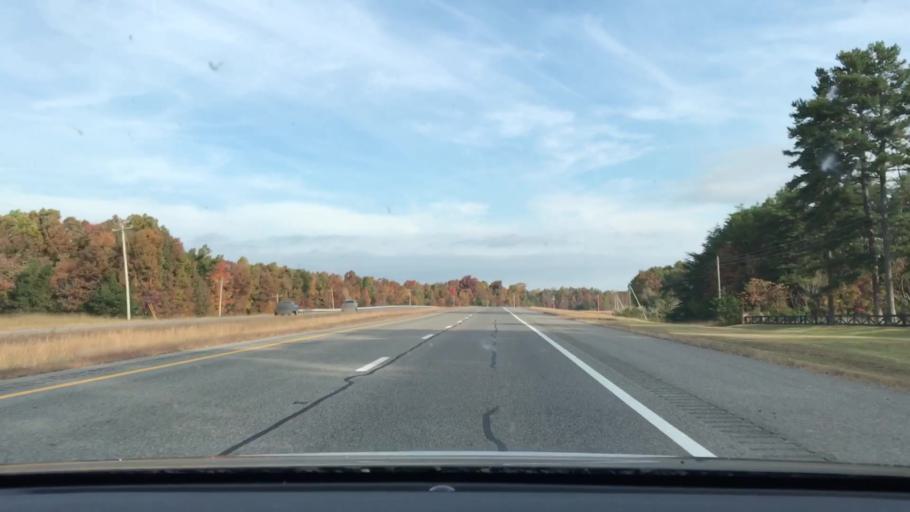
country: US
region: Tennessee
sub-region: Fentress County
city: Jamestown
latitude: 36.3464
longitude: -84.9523
